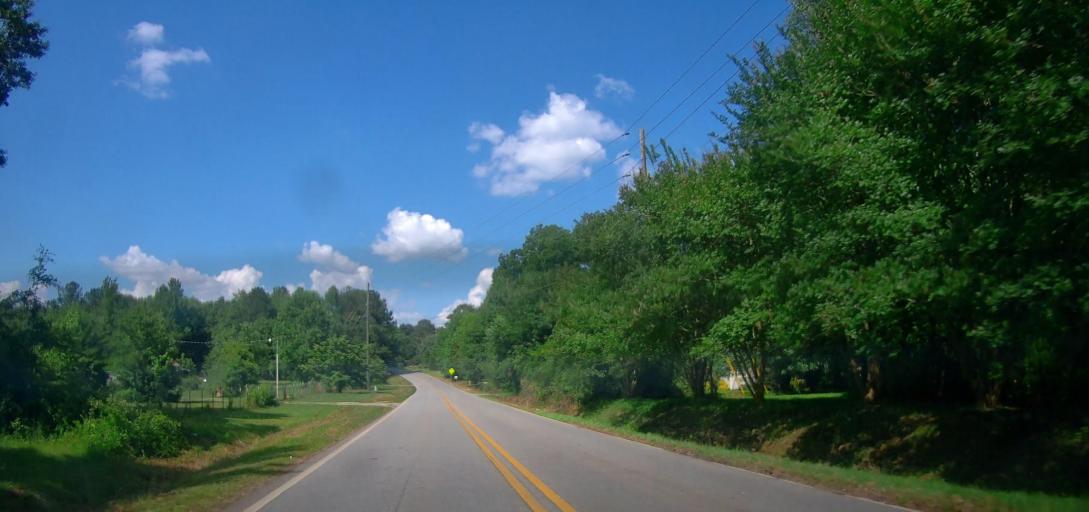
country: US
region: Georgia
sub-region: Spalding County
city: East Griffin
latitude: 33.2872
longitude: -84.2145
